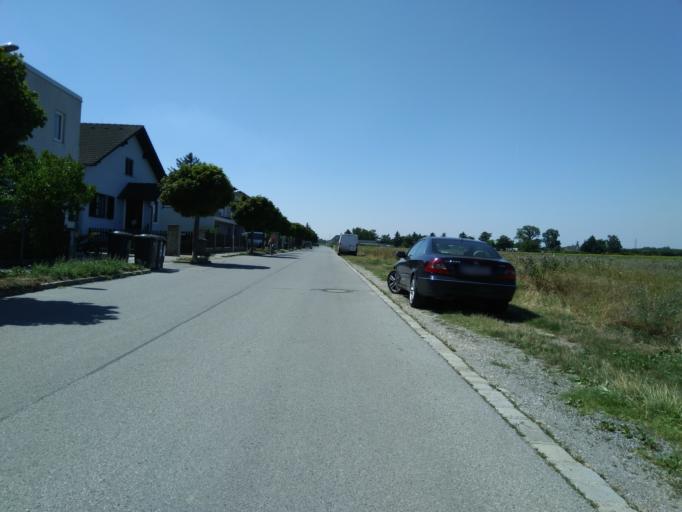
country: AT
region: Lower Austria
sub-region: Politischer Bezirk Ganserndorf
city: Deutsch-Wagram
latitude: 48.3125
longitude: 16.5670
